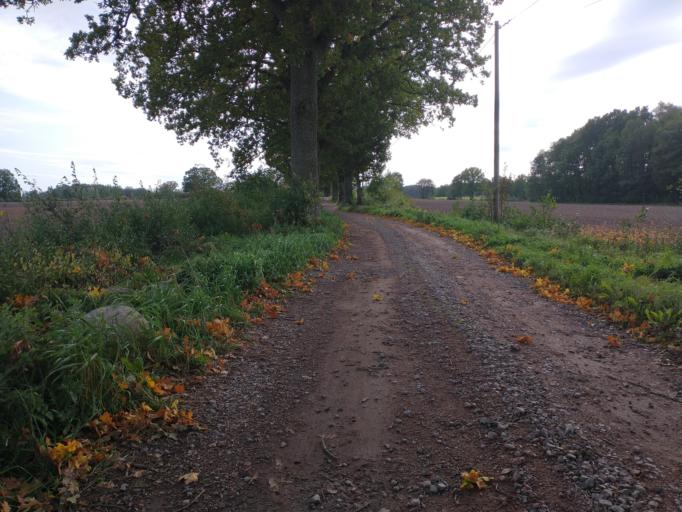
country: SE
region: Kalmar
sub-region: Kalmar Kommun
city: Lindsdal
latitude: 56.7755
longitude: 16.3078
